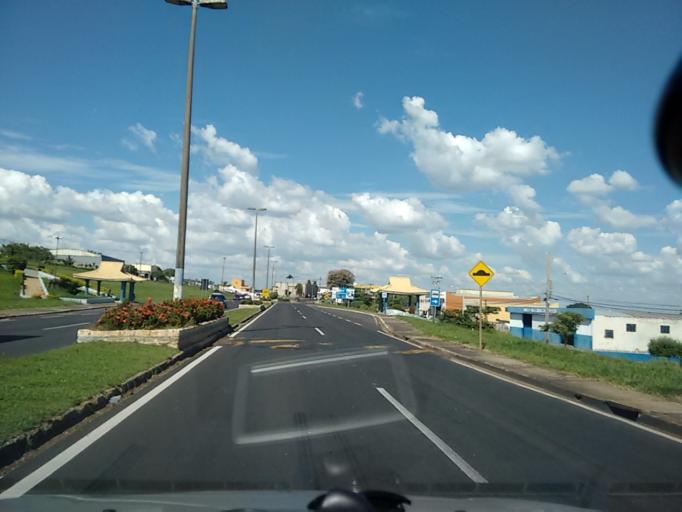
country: BR
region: Sao Paulo
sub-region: Pompeia
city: Pompeia
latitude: -22.1036
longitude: -50.1901
